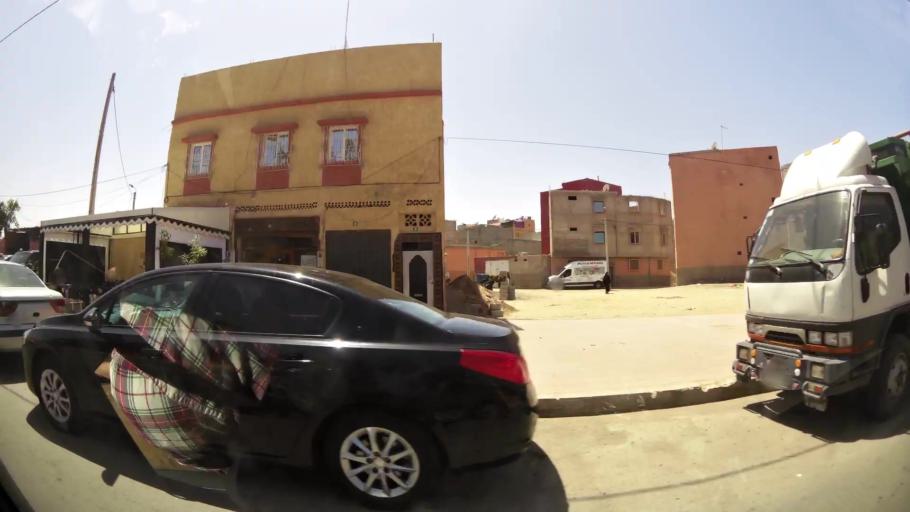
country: MA
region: Souss-Massa-Draa
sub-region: Inezgane-Ait Mellou
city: Inezgane
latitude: 30.3443
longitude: -9.4930
